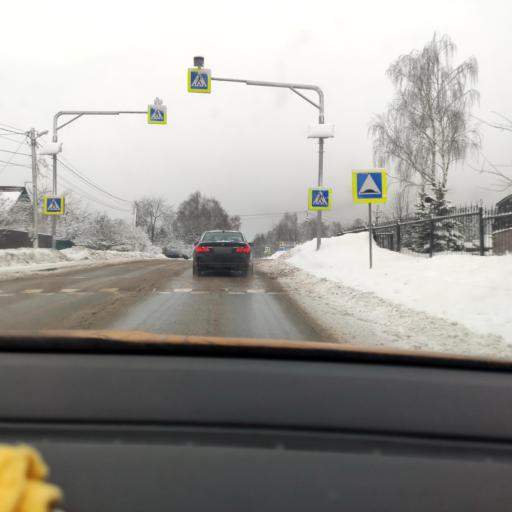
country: RU
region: Moskovskaya
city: Yershovo
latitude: 55.7690
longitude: 36.8590
